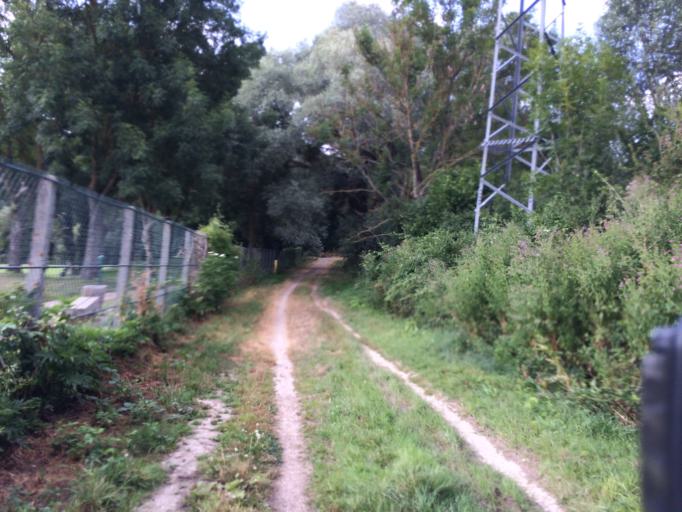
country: FR
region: Ile-de-France
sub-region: Departement de l'Essonne
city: Etiolles
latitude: 48.6396
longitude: 2.4915
